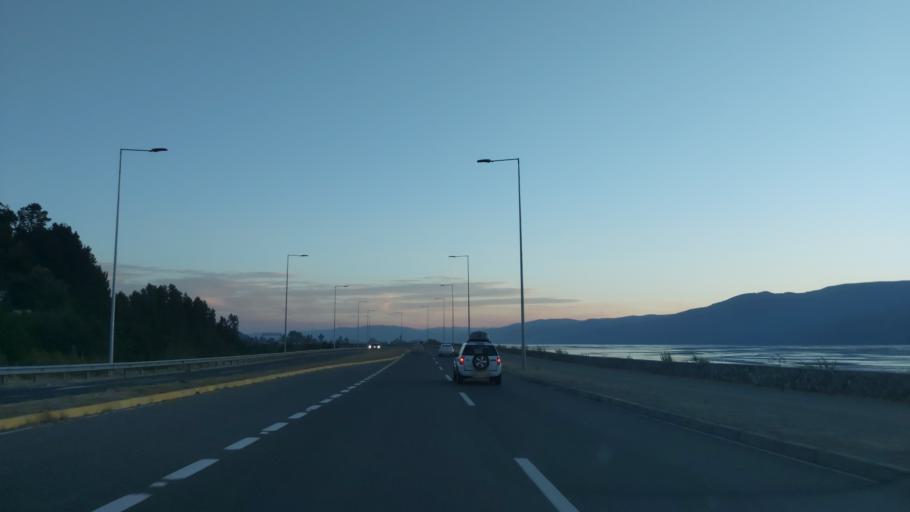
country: CL
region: Biobio
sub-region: Provincia de Concepcion
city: Concepcion
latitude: -36.8690
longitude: -73.0440
